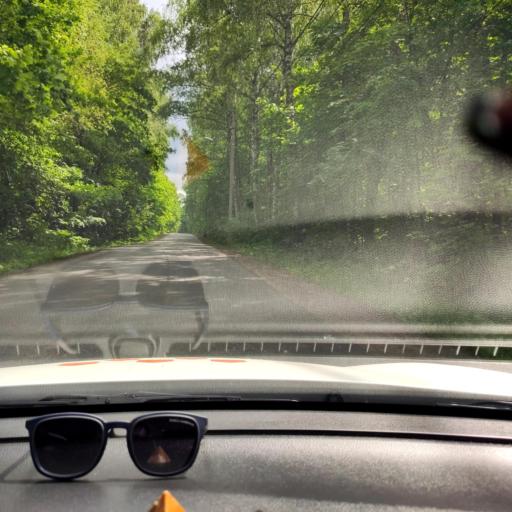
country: RU
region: Tatarstan
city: Vysokaya Gora
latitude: 55.9333
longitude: 49.1833
